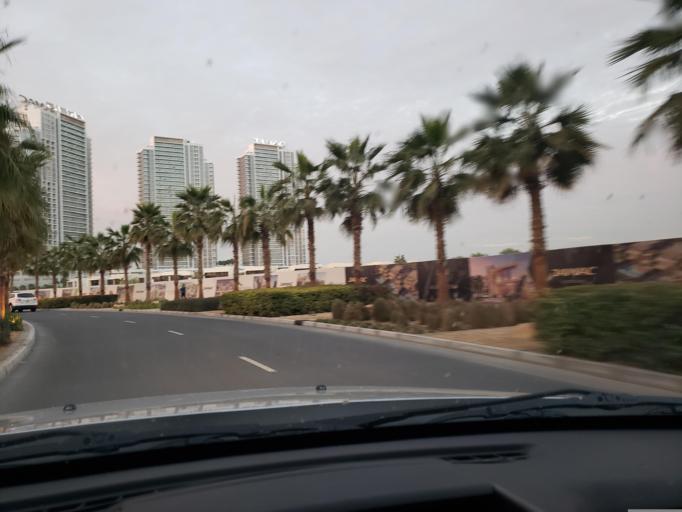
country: AE
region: Dubai
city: Dubai
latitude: 25.0210
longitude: 55.2449
